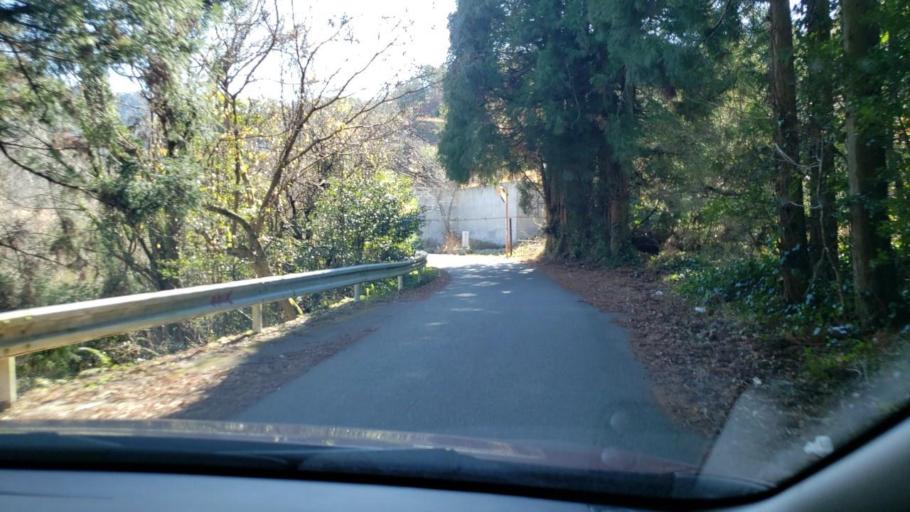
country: JP
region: Tokushima
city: Narutocho-mitsuishi
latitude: 34.2008
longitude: 134.5537
